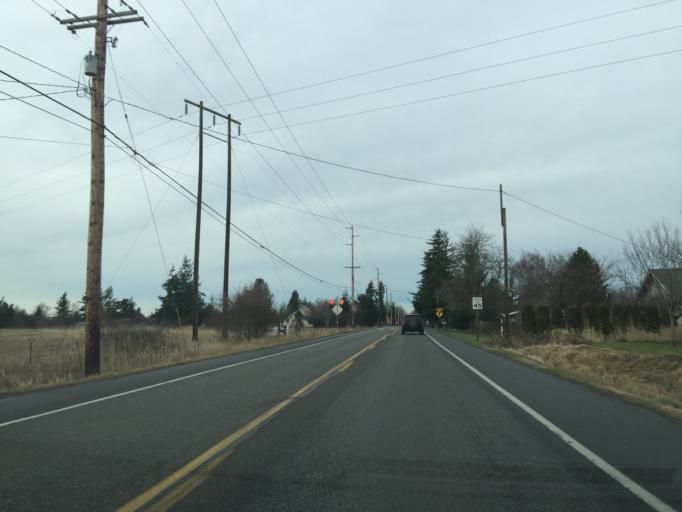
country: US
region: Washington
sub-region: Whatcom County
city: Marietta-Alderwood
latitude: 48.8174
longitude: -122.5287
